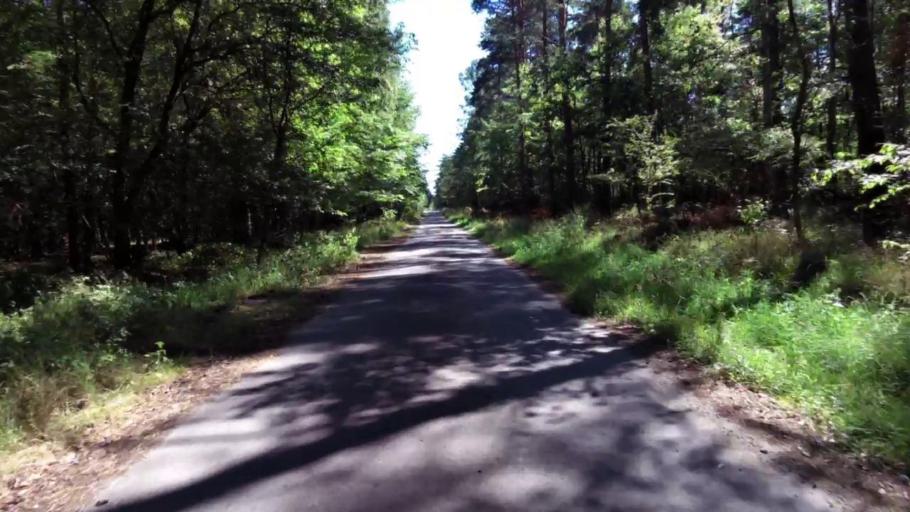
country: PL
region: West Pomeranian Voivodeship
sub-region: Powiat szczecinecki
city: Borne Sulinowo
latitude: 53.5953
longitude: 16.6392
